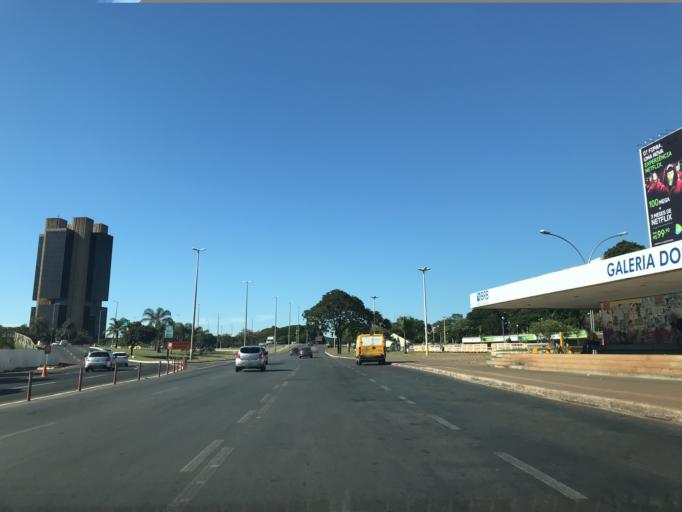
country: BR
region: Federal District
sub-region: Brasilia
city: Brasilia
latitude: -15.7986
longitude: -47.8853
